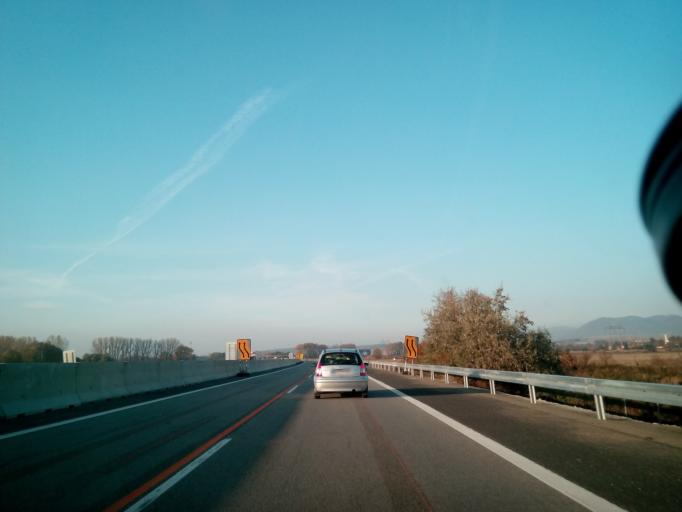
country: SK
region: Kosicky
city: Kosice
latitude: 48.8220
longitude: 21.3103
